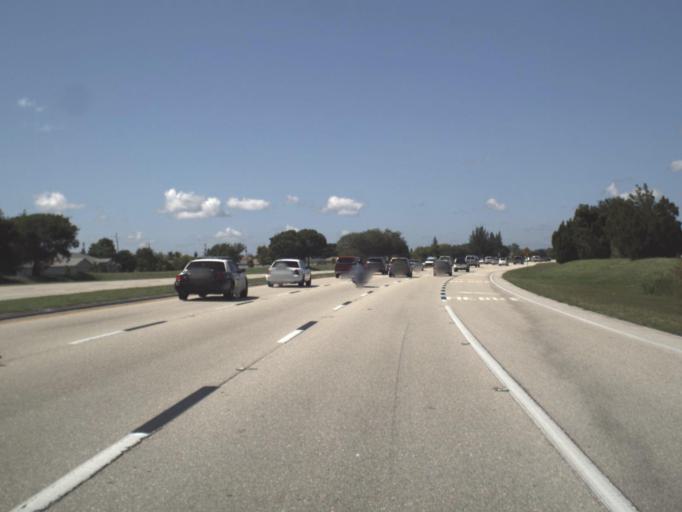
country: US
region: Florida
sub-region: Lee County
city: Cape Coral
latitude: 26.6047
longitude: -81.9598
